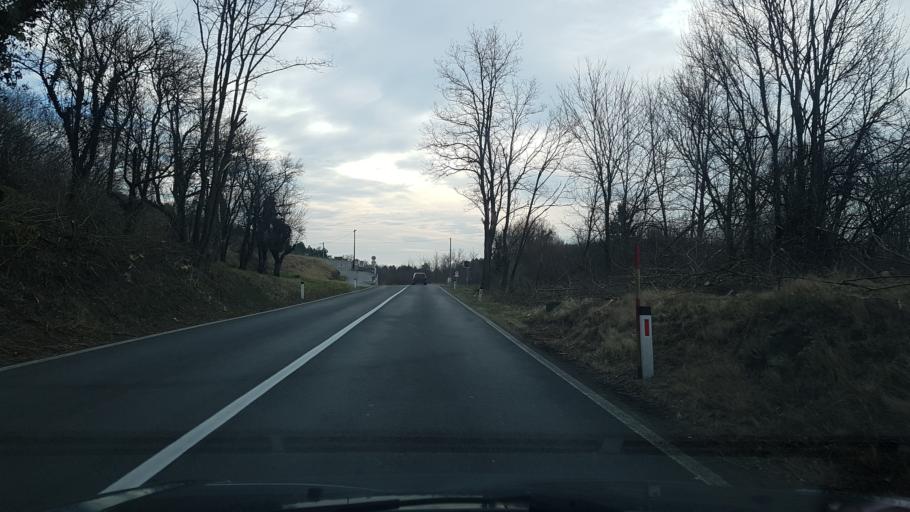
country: SI
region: Ilirska Bistrica
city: Ilirska Bistrica
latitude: 45.4973
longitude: 14.1888
